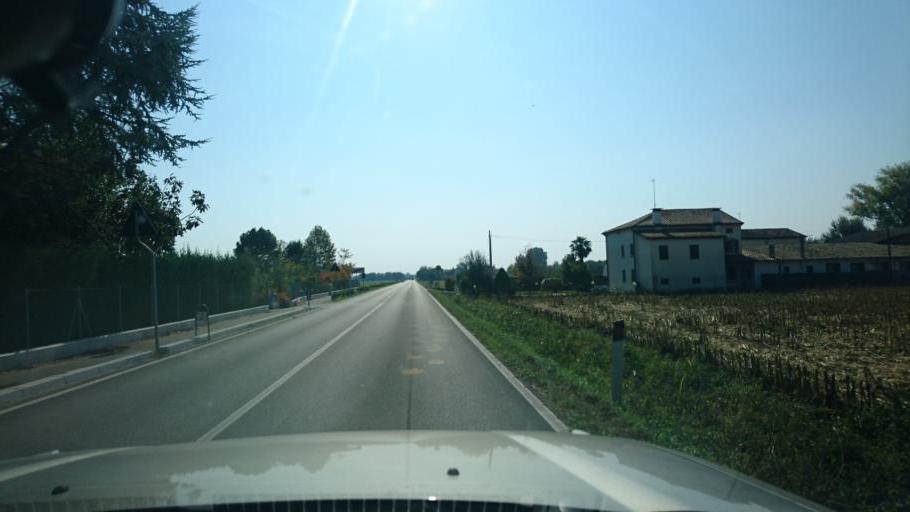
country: IT
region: Veneto
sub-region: Provincia di Padova
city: Gazzo
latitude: 45.5777
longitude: 11.7085
